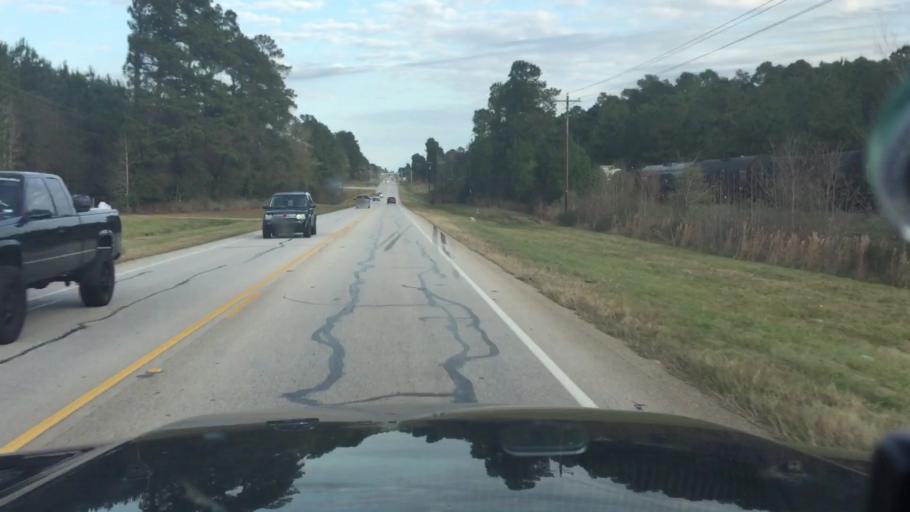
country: US
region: Texas
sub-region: Montgomery County
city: Panorama Village
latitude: 30.3183
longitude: -95.6107
